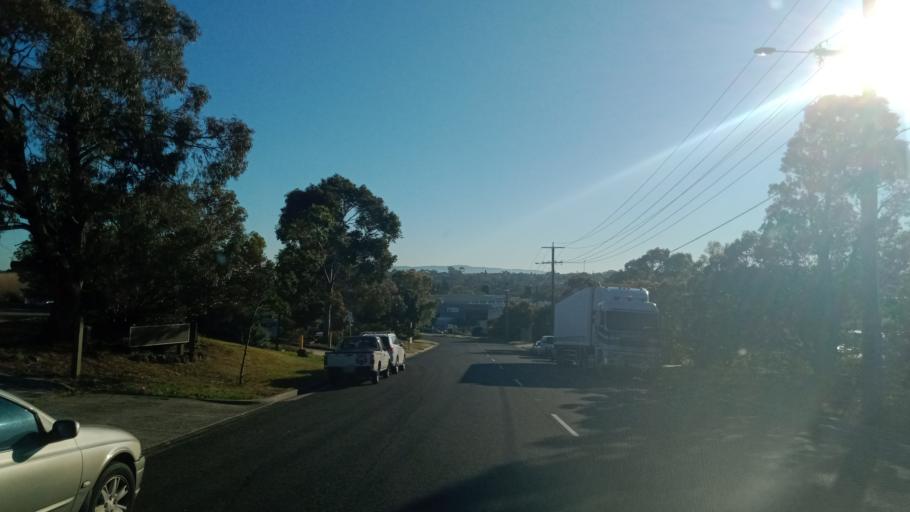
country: AU
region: Victoria
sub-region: Greater Dandenong
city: Noble Park North
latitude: -37.9549
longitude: 145.1867
